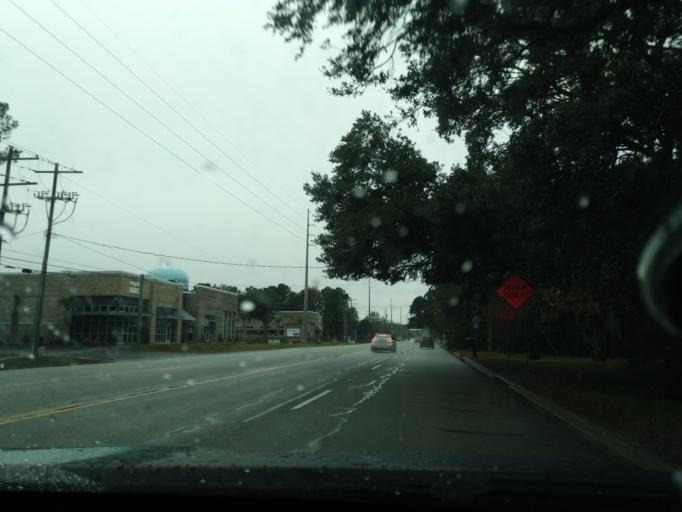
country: US
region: South Carolina
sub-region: Charleston County
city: Folly Beach
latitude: 32.7136
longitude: -79.9648
